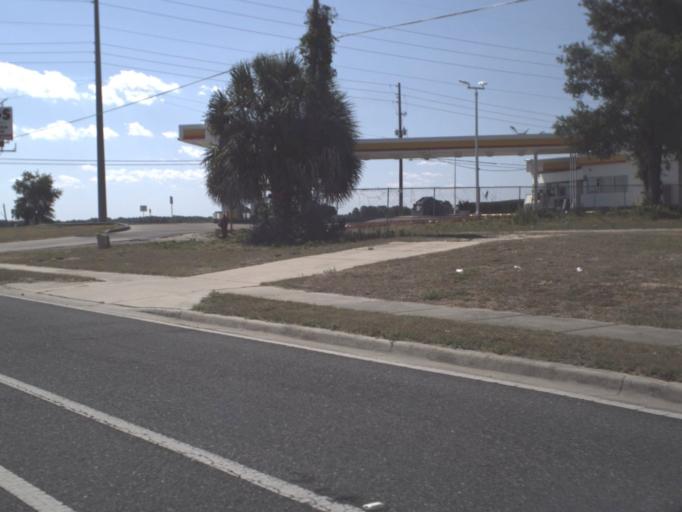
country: US
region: Florida
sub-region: Marion County
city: Ocala
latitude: 29.1866
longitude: -82.2175
